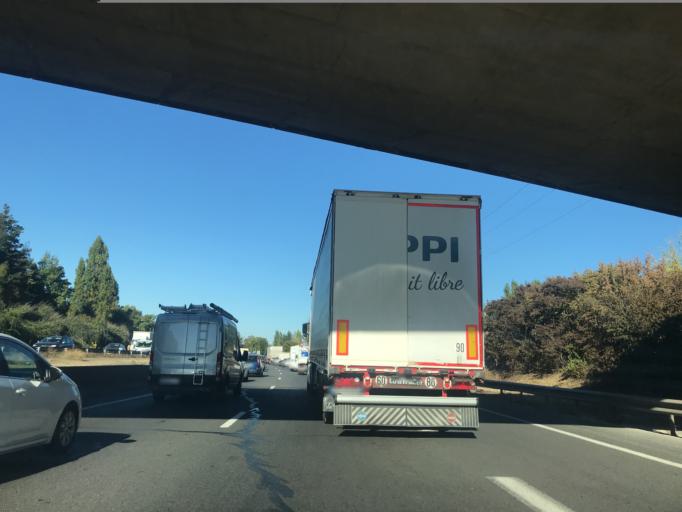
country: FR
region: Aquitaine
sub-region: Departement de la Gironde
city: Bruges
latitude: 44.8821
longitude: -0.6236
